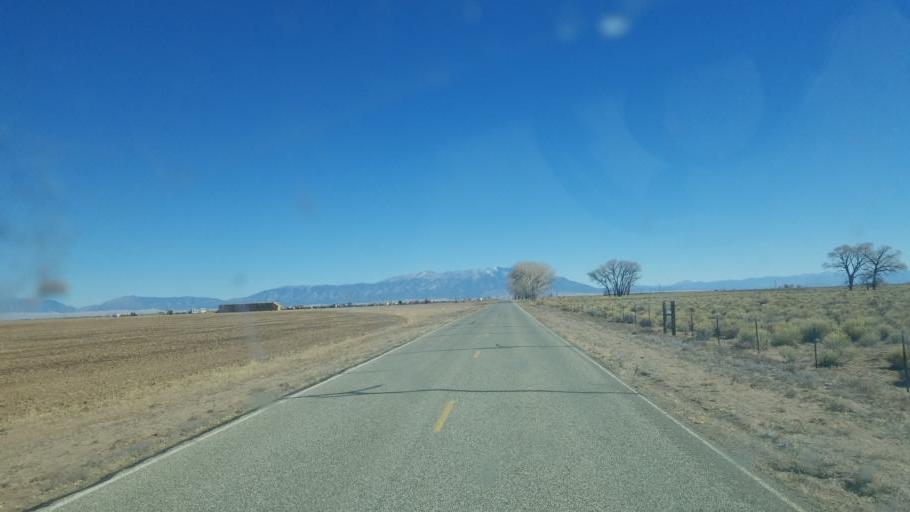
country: US
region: Colorado
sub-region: Alamosa County
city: Alamosa
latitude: 37.5742
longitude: -105.9709
